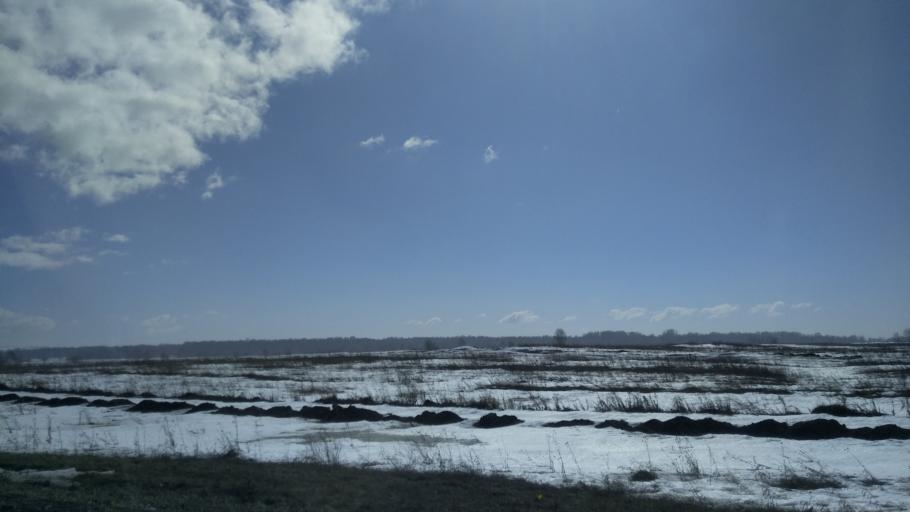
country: RU
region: Kemerovo
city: Yurga
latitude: 55.6834
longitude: 85.0055
